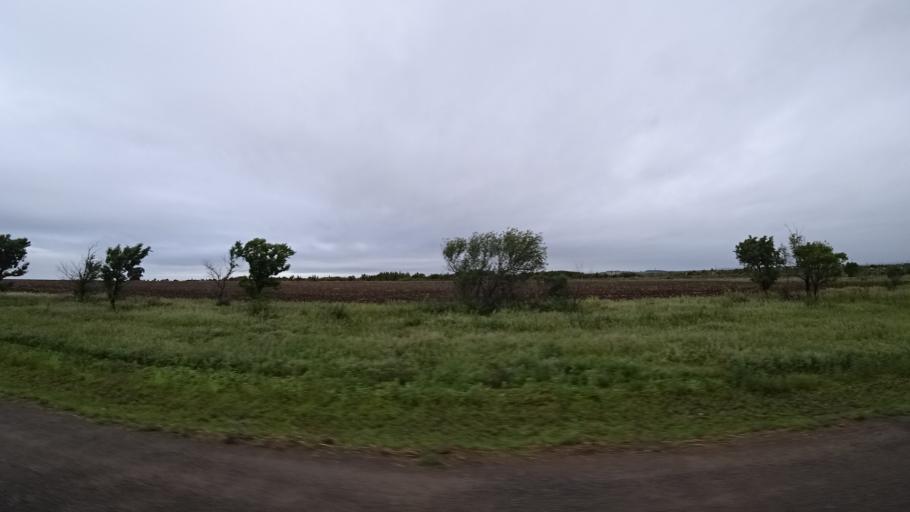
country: RU
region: Primorskiy
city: Chernigovka
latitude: 44.3204
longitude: 132.5674
